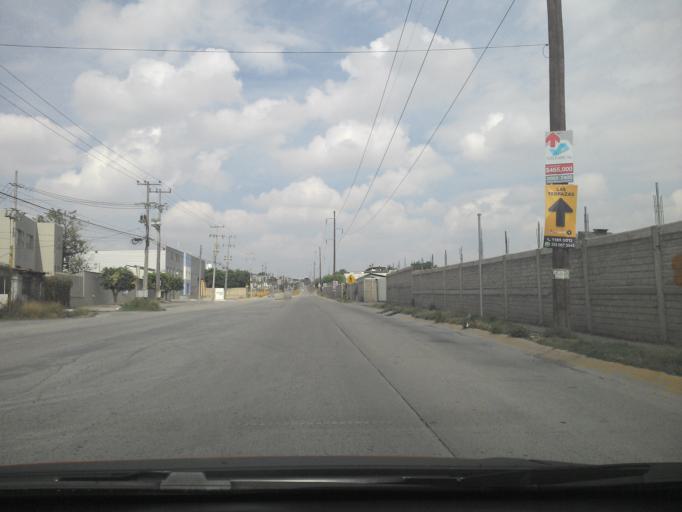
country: MX
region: Jalisco
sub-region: Tlajomulco de Zuniga
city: Altus Bosques
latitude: 20.5776
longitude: -103.3572
